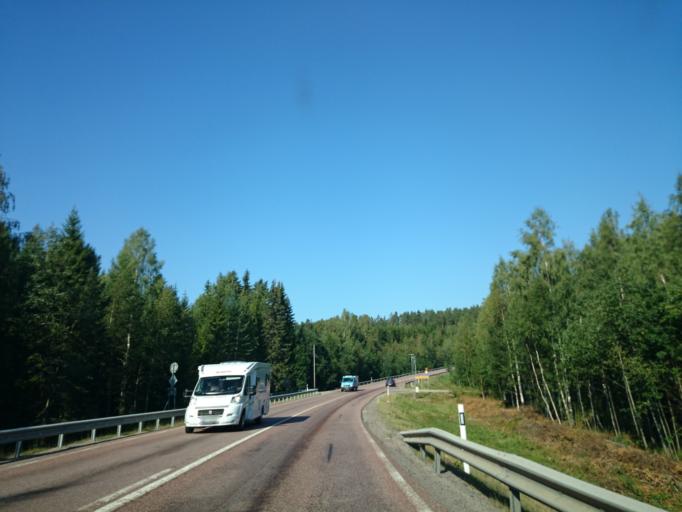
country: SE
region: Gaevleborg
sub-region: Hudiksvalls Kommun
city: Sorforsa
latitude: 61.7578
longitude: 16.7904
